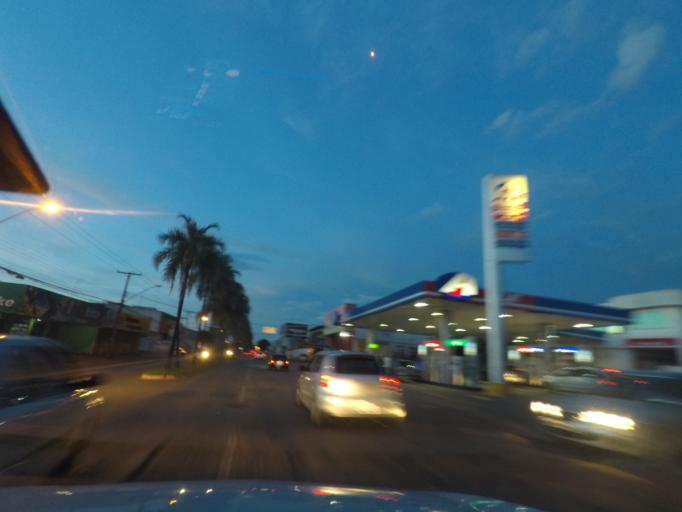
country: BR
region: Goias
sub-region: Goiania
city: Goiania
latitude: -16.7073
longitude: -49.3149
